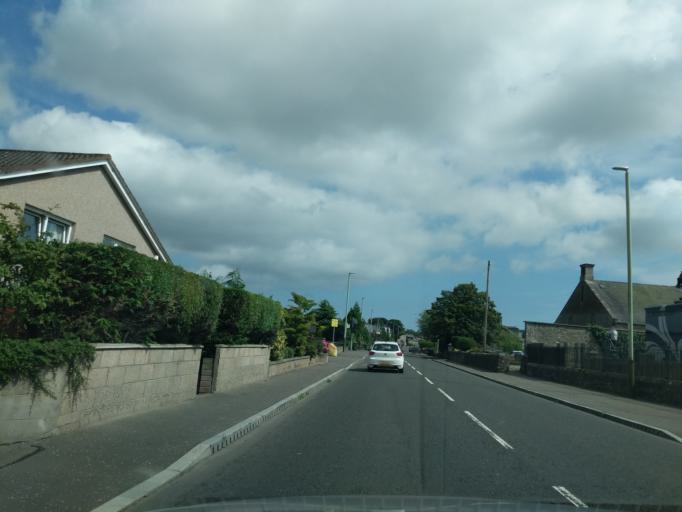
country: GB
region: Scotland
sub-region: Angus
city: Muirhead
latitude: 56.4979
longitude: -3.0718
